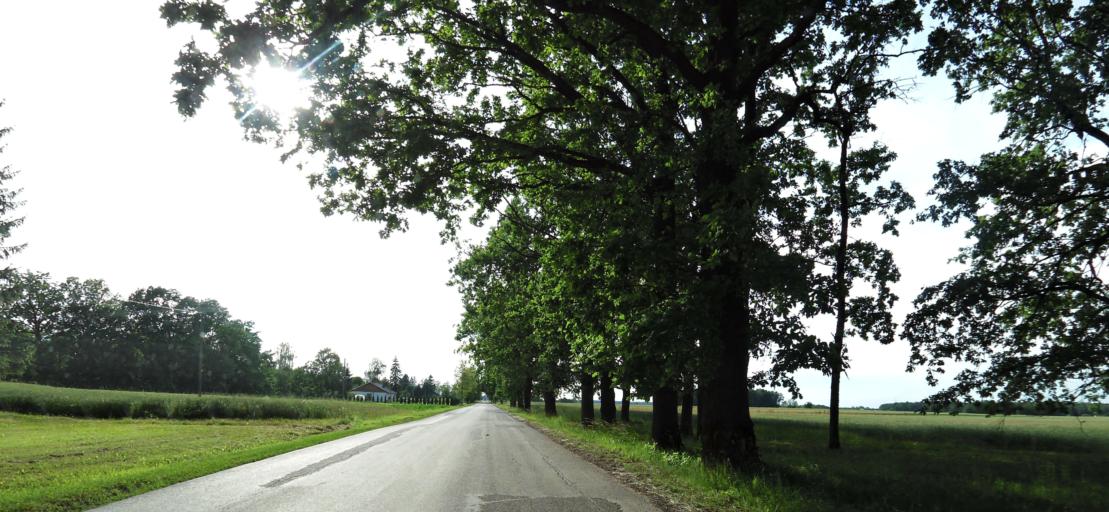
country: LT
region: Panevezys
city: Pasvalys
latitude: 56.1075
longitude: 24.4779
